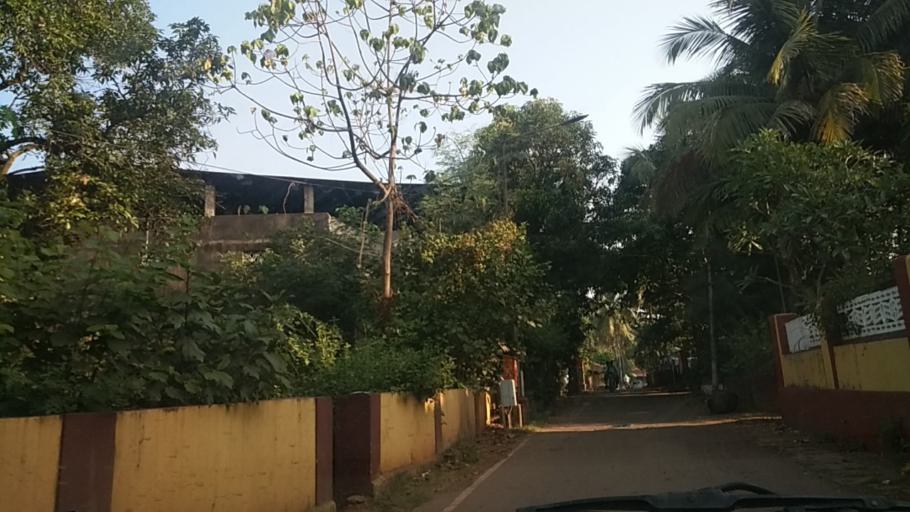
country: IN
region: Goa
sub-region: South Goa
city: Madgaon
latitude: 15.2758
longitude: 73.9534
